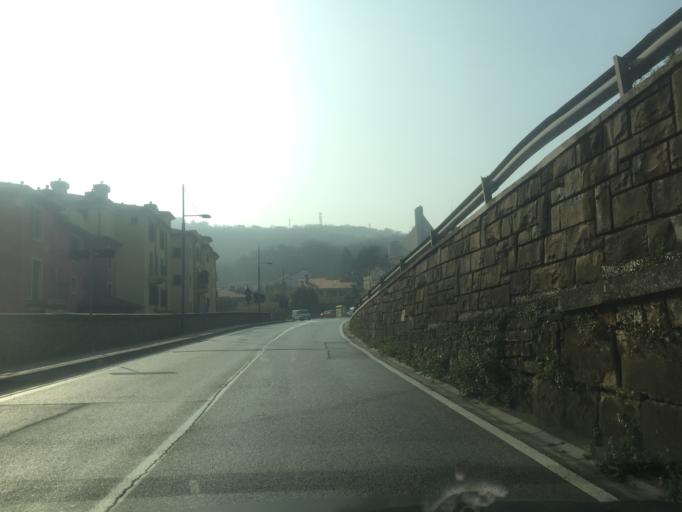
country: IT
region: Friuli Venezia Giulia
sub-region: Provincia di Trieste
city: Muggia
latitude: 45.6078
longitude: 13.7506
